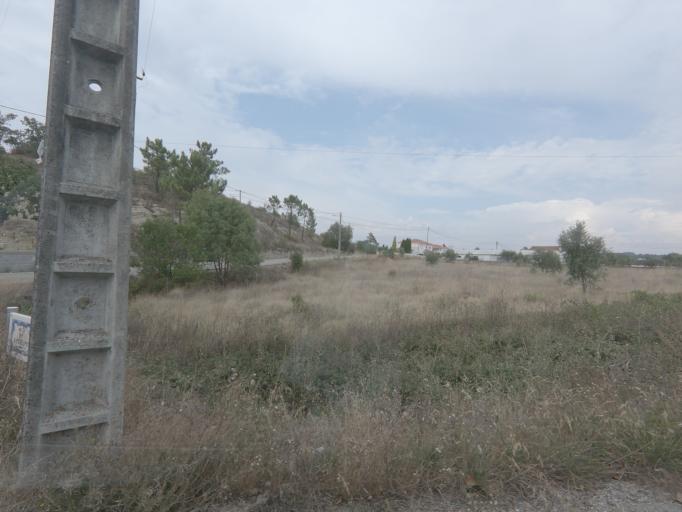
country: PT
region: Coimbra
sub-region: Condeixa-A-Nova
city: Condeixa-a-Nova
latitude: 40.1398
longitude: -8.4650
